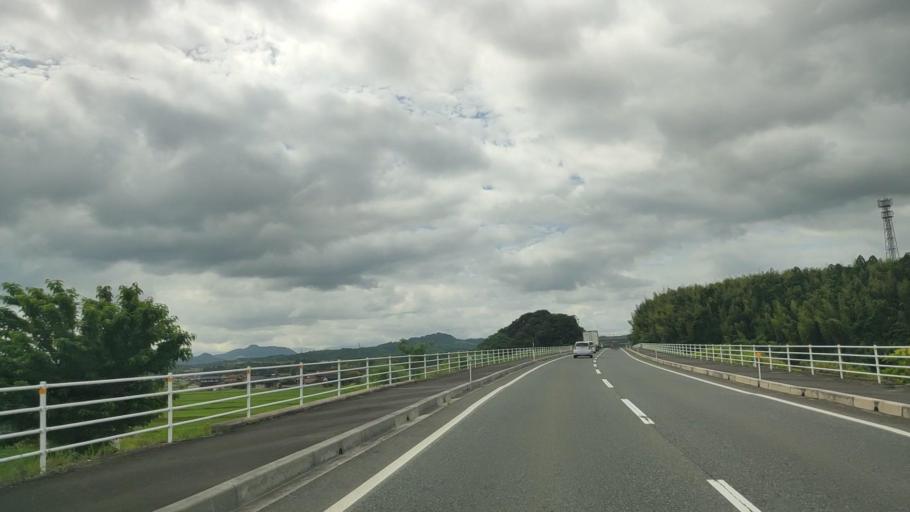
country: JP
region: Tottori
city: Yonago
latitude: 35.3948
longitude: 133.3816
